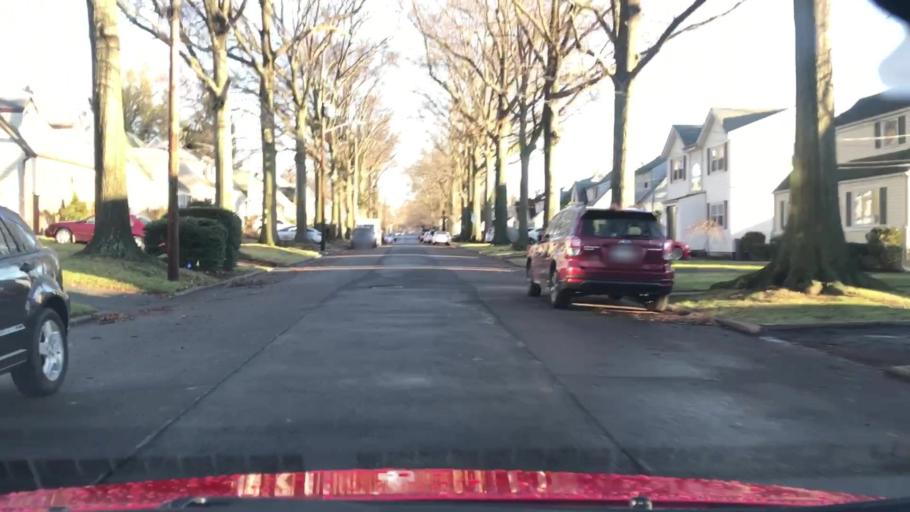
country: US
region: New Jersey
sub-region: Bergen County
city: Leonia
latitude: 40.8783
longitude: -74.0036
